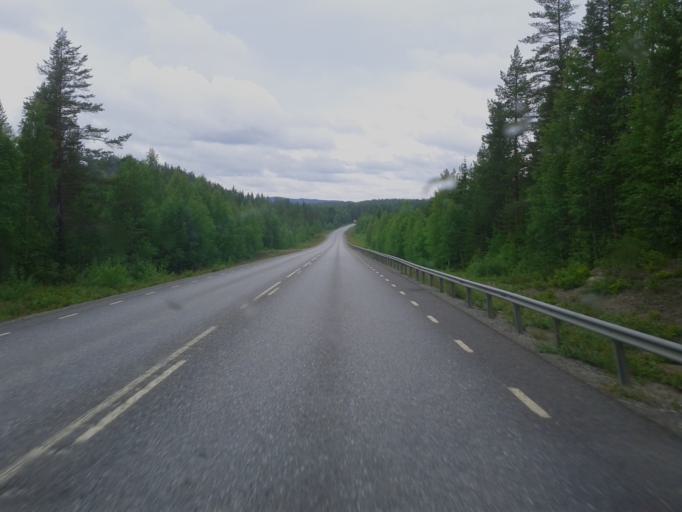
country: SE
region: Vaesterbotten
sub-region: Skelleftea Kommun
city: Langsele
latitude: 64.8927
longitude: 20.1704
